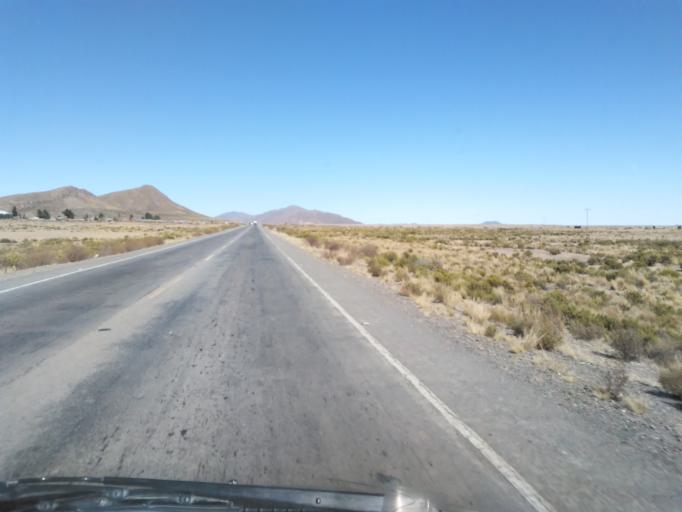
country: BO
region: Oruro
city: Machacamarca
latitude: -18.0992
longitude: -67.0084
